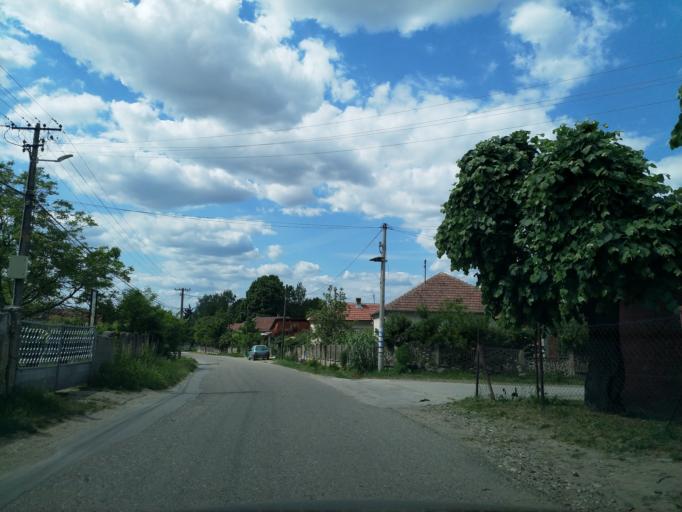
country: RS
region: Central Serbia
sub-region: Pomoravski Okrug
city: Jagodina
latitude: 43.9427
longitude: 21.2987
